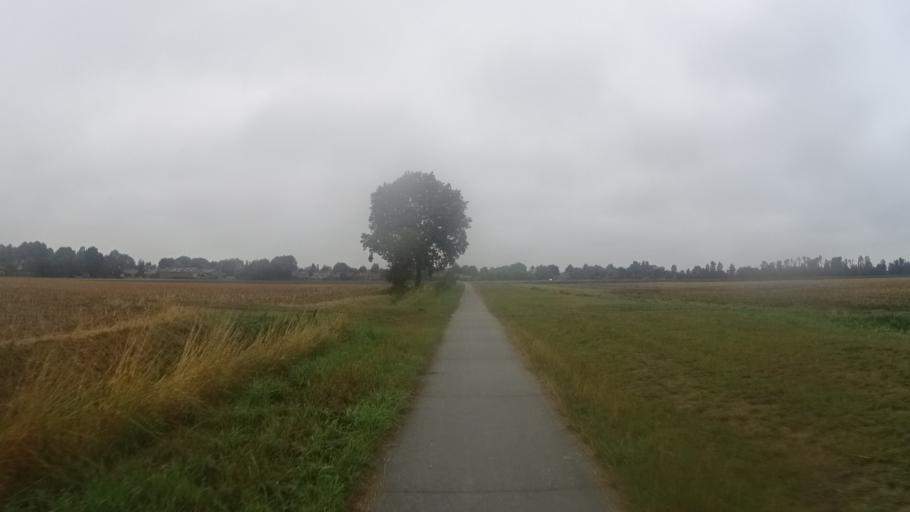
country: NL
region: Groningen
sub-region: Gemeente Slochteren
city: Slochteren
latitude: 53.1882
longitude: 6.8785
